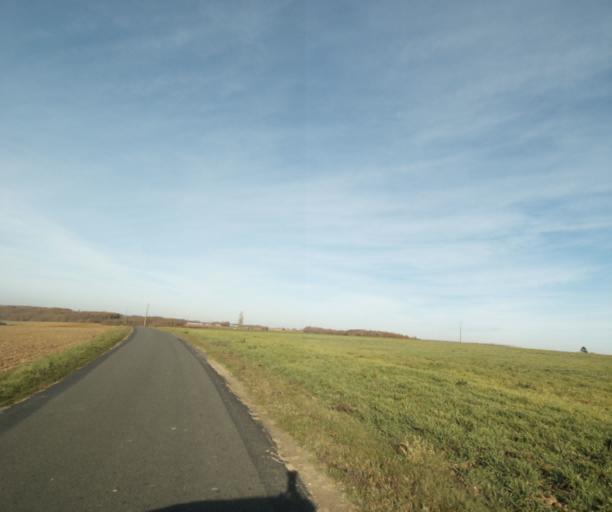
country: FR
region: Poitou-Charentes
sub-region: Departement de la Charente-Maritime
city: Chaniers
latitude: 45.7201
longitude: -0.5288
